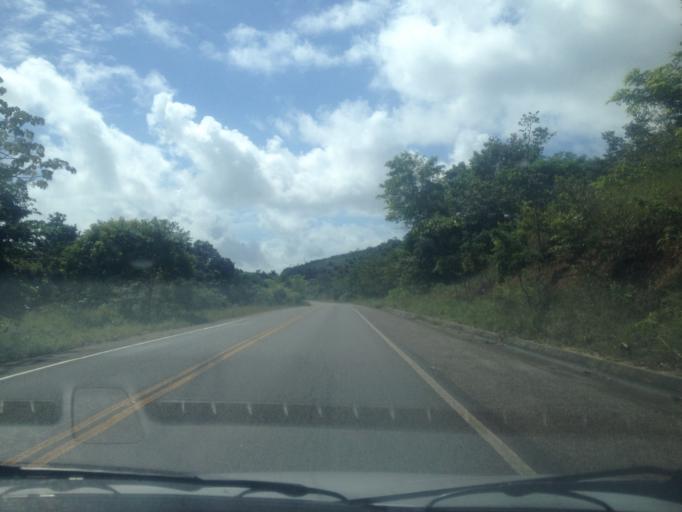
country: BR
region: Bahia
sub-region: Conde
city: Conde
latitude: -12.0323
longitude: -37.7001
